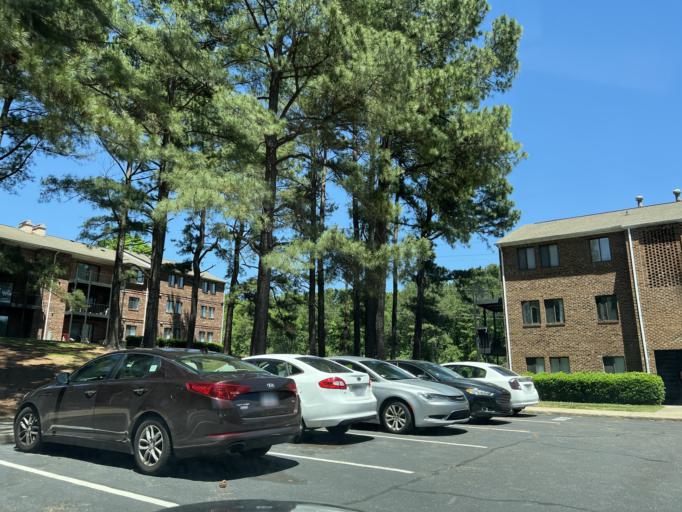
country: US
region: North Carolina
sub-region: Wake County
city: Raleigh
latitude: 35.8535
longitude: -78.5720
